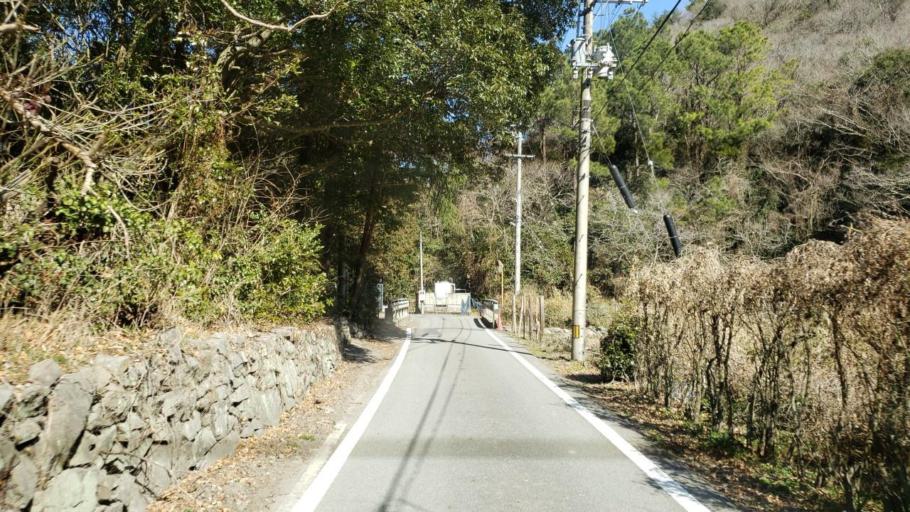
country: JP
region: Tokushima
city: Narutocho-mitsuishi
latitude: 34.1767
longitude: 134.5461
